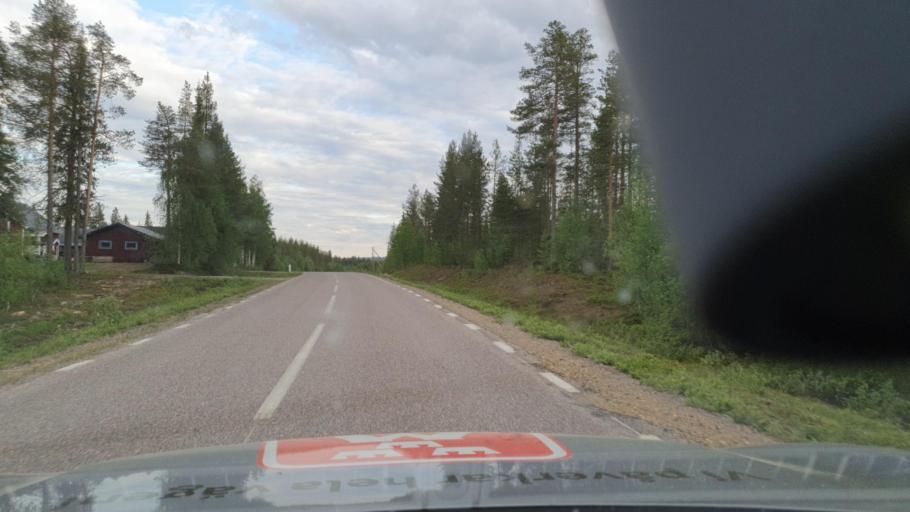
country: SE
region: Norrbotten
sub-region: Gallivare Kommun
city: Gaellivare
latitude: 66.9944
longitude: 21.2806
